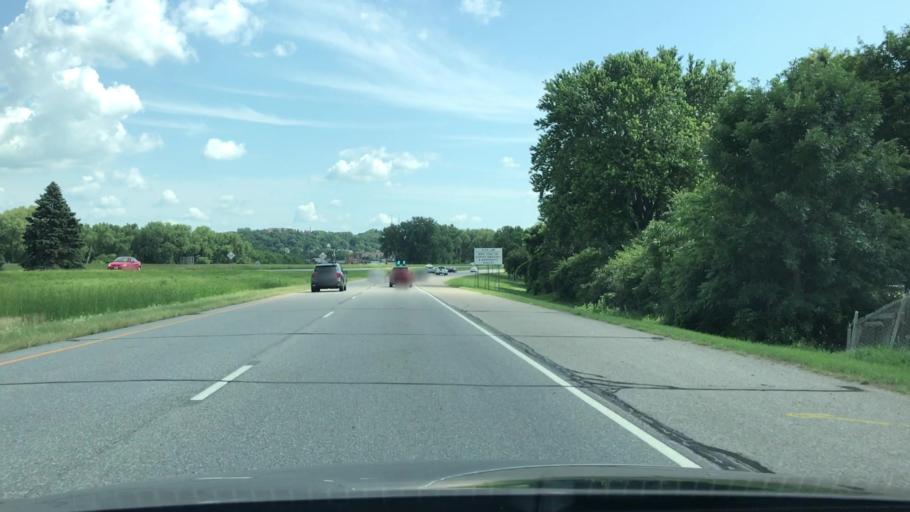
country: US
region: Minnesota
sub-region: Blue Earth County
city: Mankato
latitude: 44.1793
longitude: -94.0060
